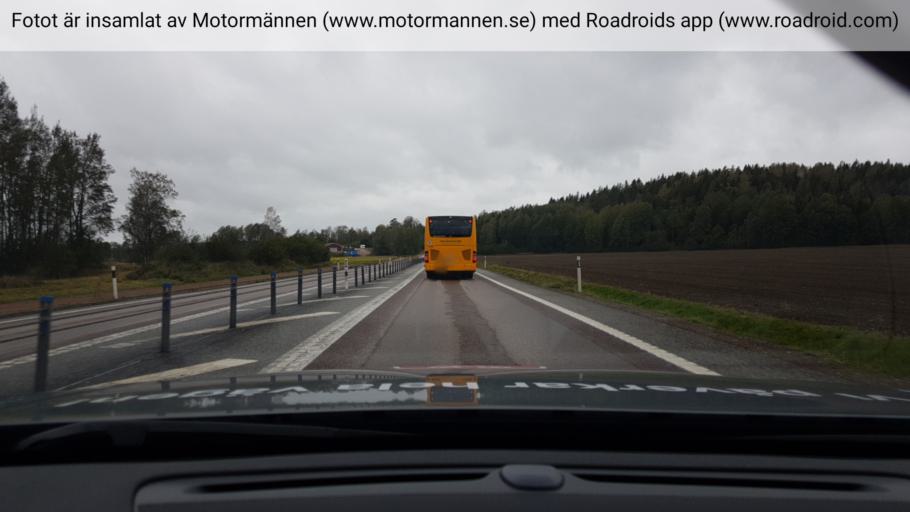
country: SE
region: Vaermland
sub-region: Kristinehamns Kommun
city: Kristinehamn
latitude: 59.3748
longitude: 13.9656
